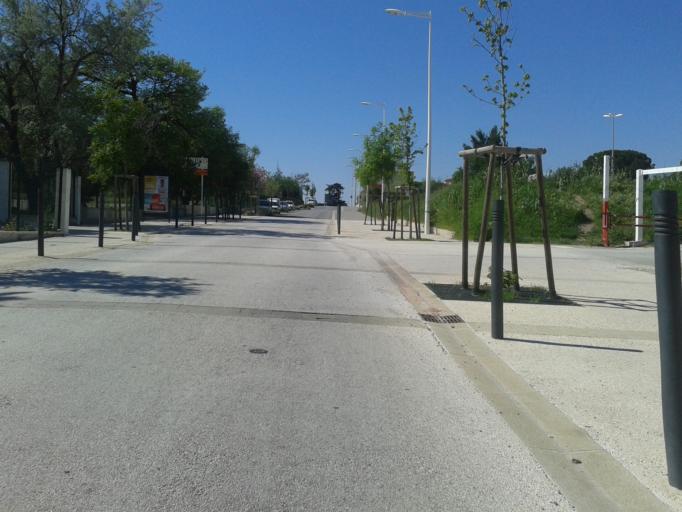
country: FR
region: Languedoc-Roussillon
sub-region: Departement des Pyrenees-Orientales
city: Perpignan
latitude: 42.6834
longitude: 2.8973
